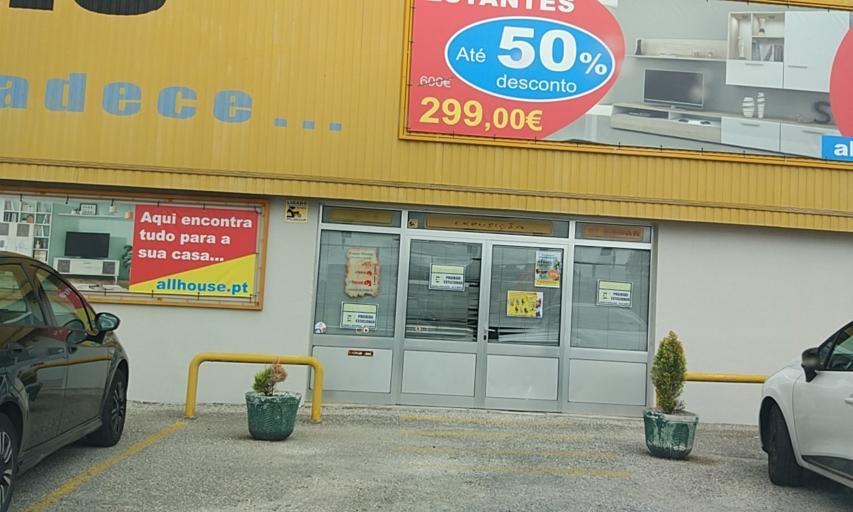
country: PT
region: Leiria
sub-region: Leiria
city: Leiria
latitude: 39.7308
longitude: -8.8239
